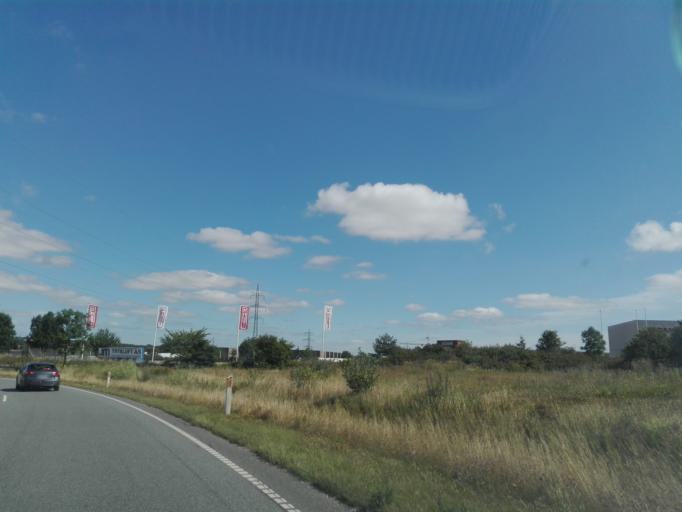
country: DK
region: Central Jutland
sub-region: Arhus Kommune
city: Trige
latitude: 56.2083
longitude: 10.1739
